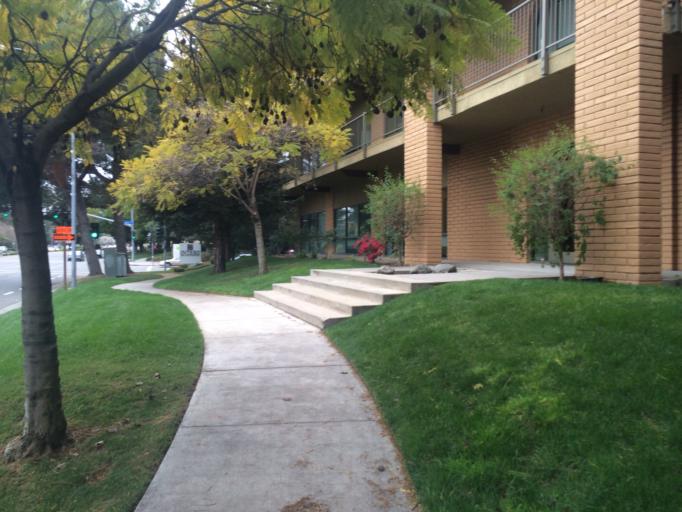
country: US
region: California
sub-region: Santa Clara County
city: Cupertino
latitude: 37.3271
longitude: -122.0326
